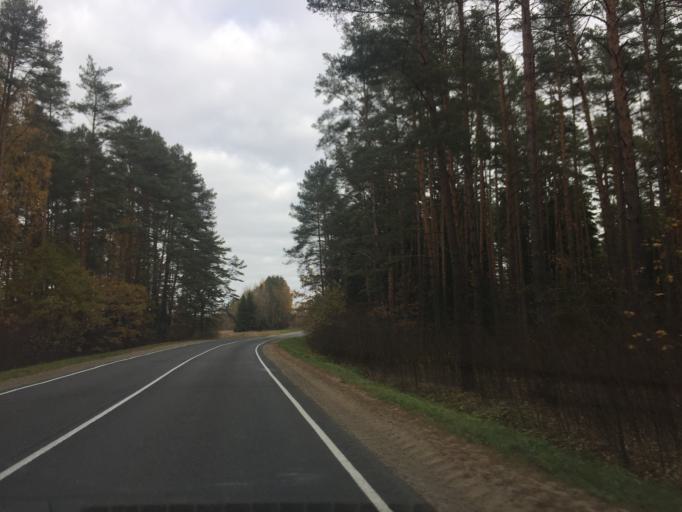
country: BY
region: Minsk
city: Svir
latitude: 54.8218
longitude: 26.1833
